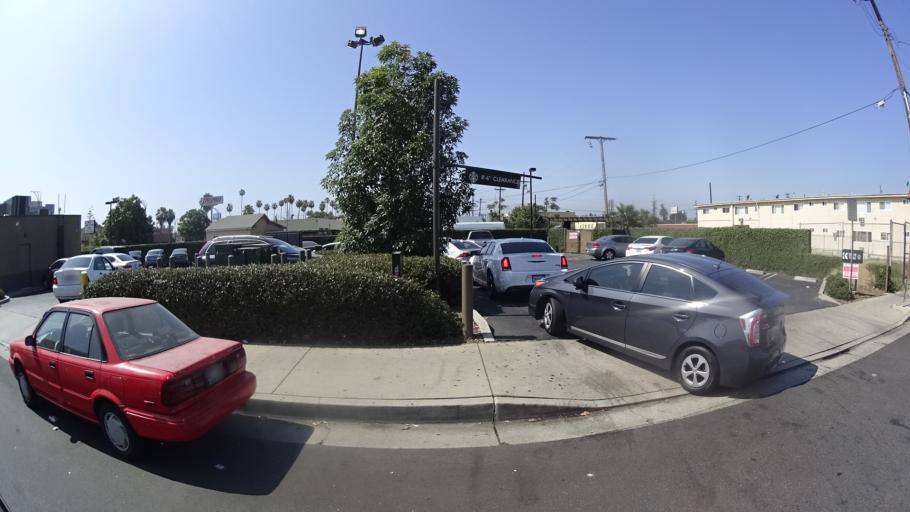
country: US
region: California
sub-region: Los Angeles County
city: Van Nuys
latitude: 34.1951
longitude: -118.4495
